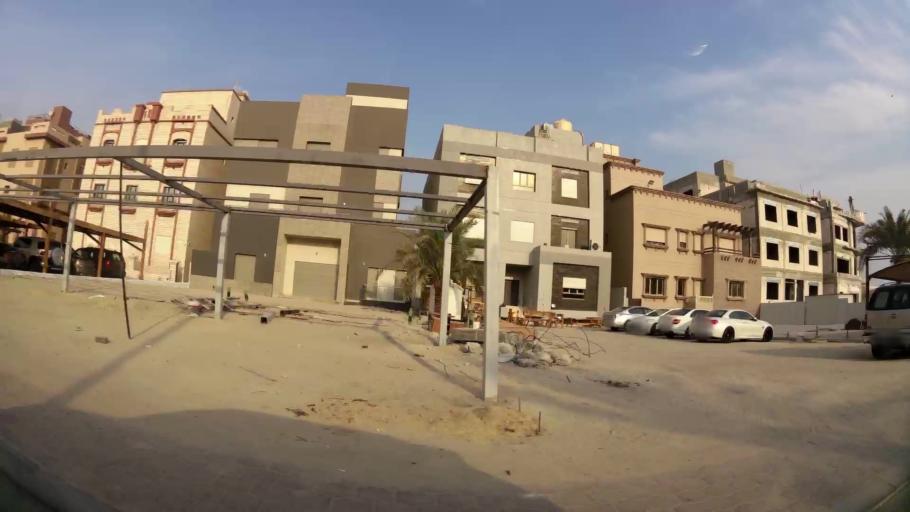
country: KW
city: Al Funaytis
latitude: 29.2330
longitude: 48.0846
